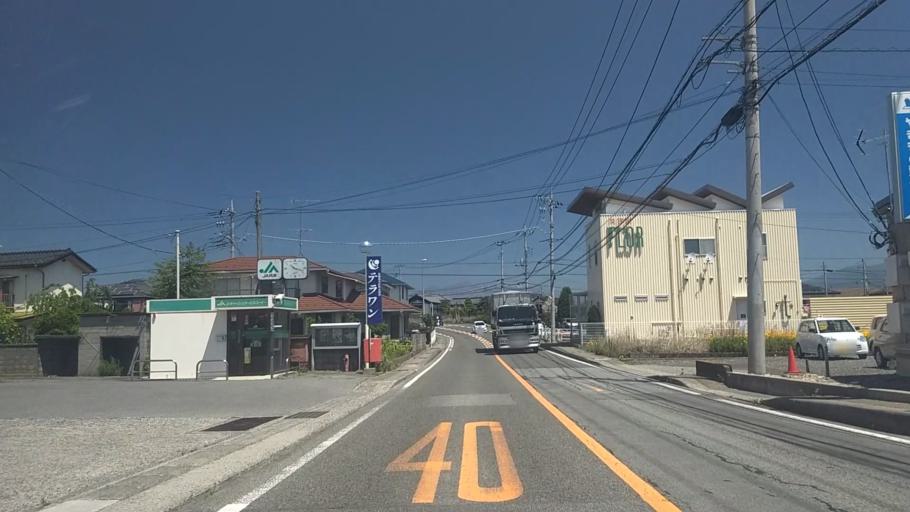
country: JP
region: Yamanashi
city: Nirasaki
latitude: 35.6803
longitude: 138.4642
